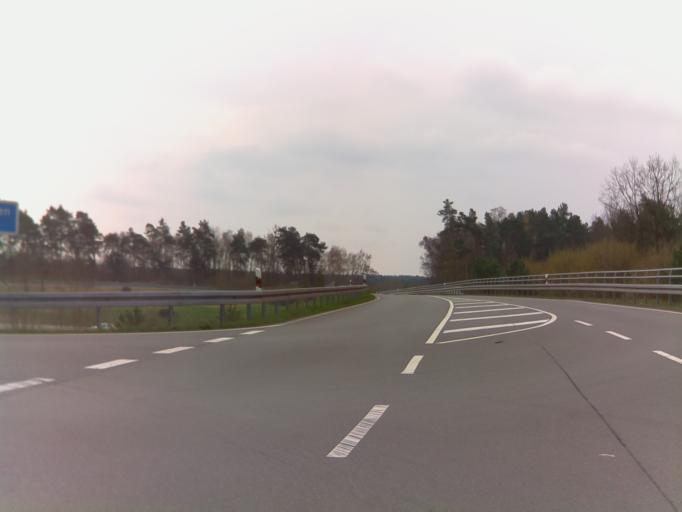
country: DE
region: Saxony-Anhalt
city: Coswig
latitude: 51.9628
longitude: 12.4638
